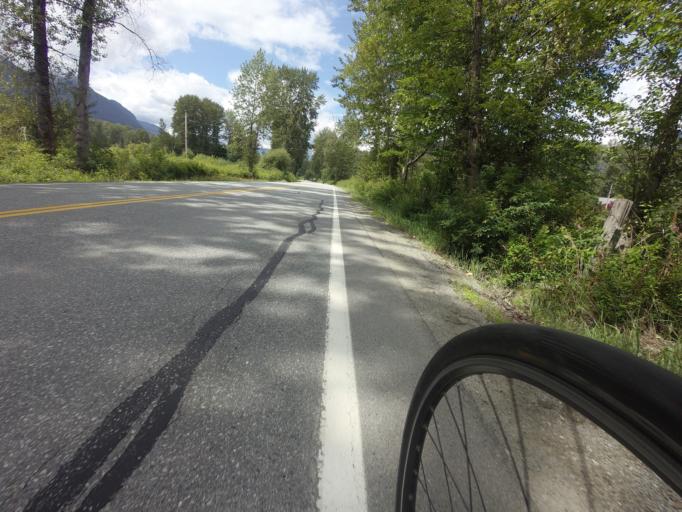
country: CA
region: British Columbia
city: Pemberton
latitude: 50.3082
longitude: -122.6339
